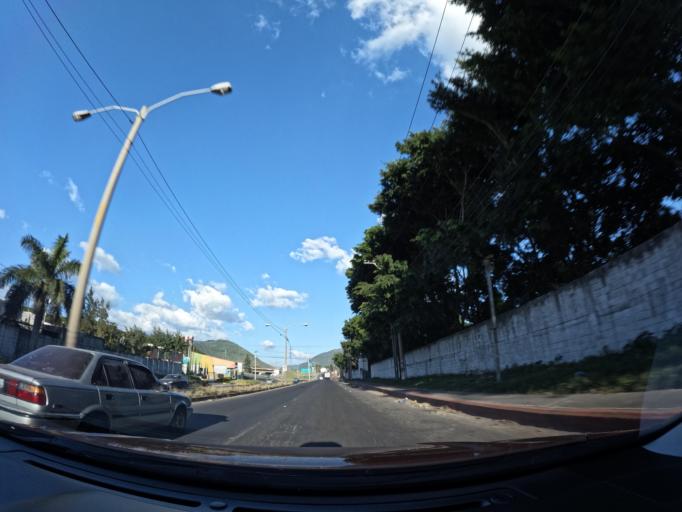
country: GT
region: Escuintla
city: Palin
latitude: 14.4093
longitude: -90.6846
